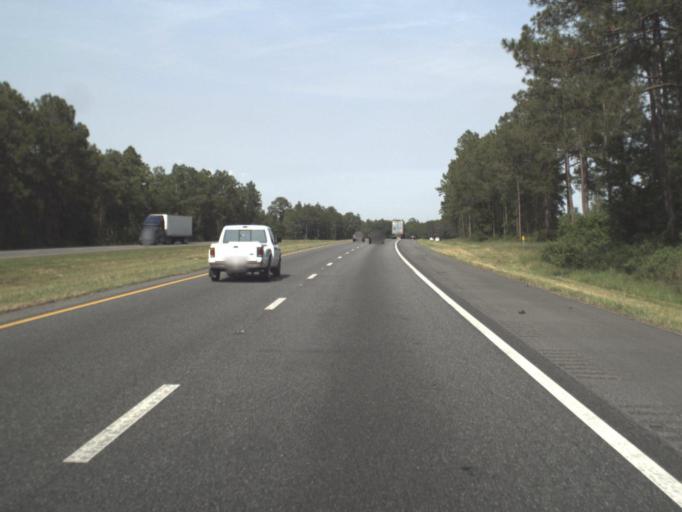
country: US
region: Florida
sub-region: Baker County
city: Macclenny
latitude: 30.2766
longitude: -82.0721
